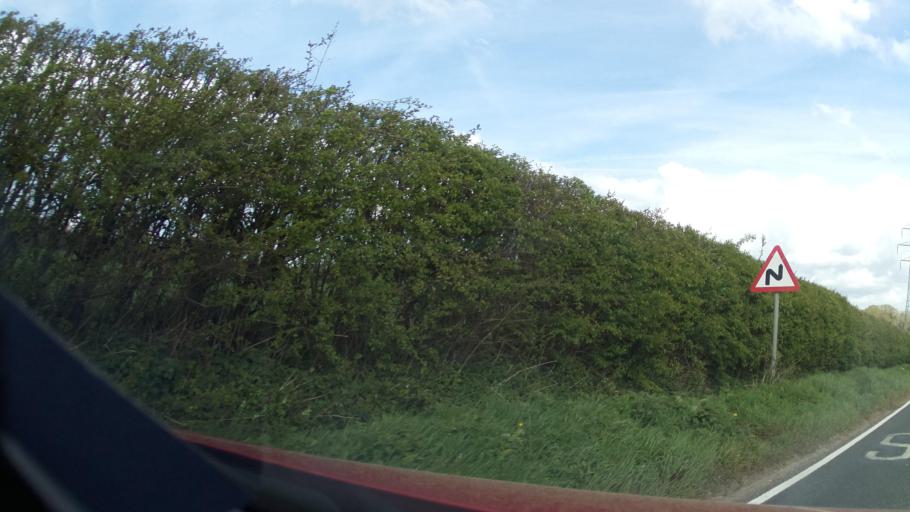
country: GB
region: England
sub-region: Hampshire
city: Compton
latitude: 51.0155
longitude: -1.3596
